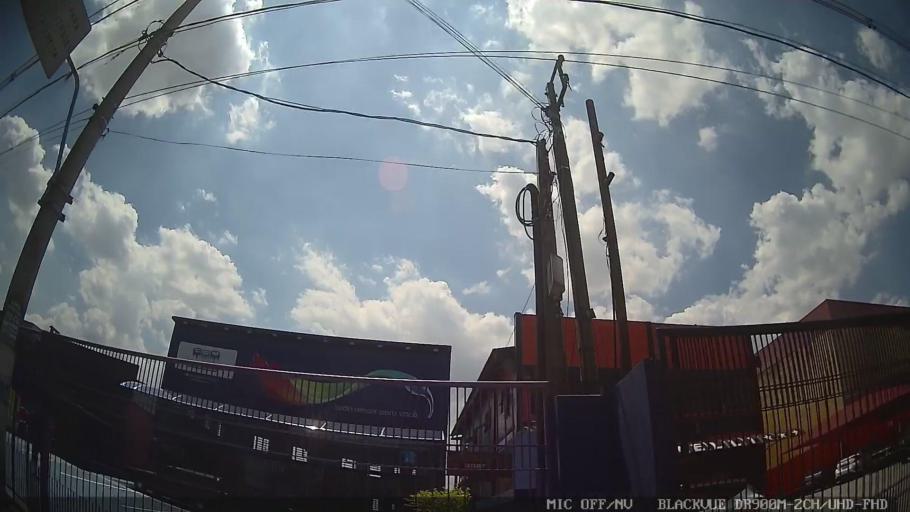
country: BR
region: Sao Paulo
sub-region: Taboao Da Serra
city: Taboao da Serra
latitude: -23.6629
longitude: -46.7808
